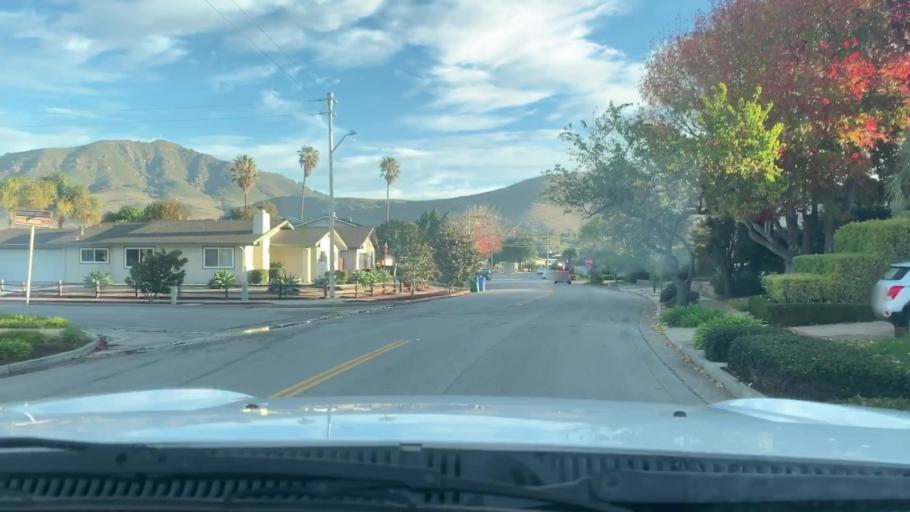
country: US
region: California
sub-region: San Luis Obispo County
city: San Luis Obispo
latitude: 35.2631
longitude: -120.6911
